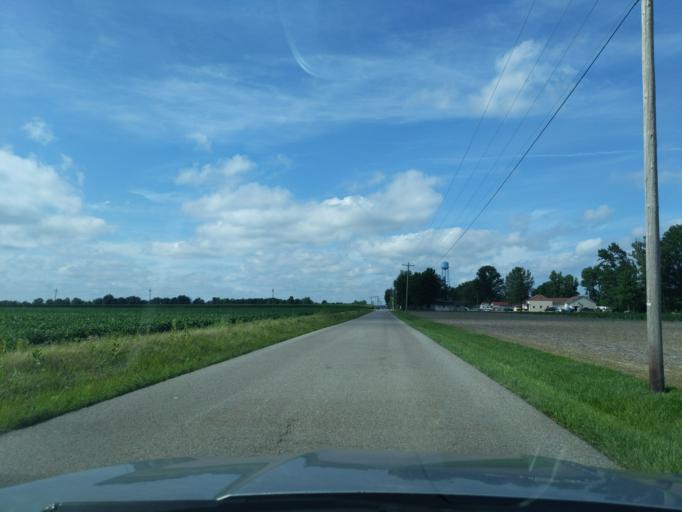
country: US
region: Indiana
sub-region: Ripley County
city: Batesville
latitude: 39.3058
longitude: -85.3477
